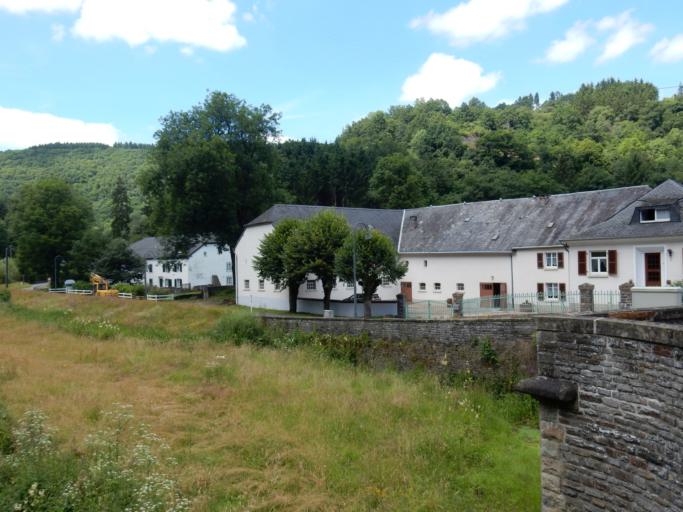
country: LU
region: Diekirch
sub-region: Canton de Wiltz
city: Wilwerwiltz
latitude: 49.9517
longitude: 6.0165
